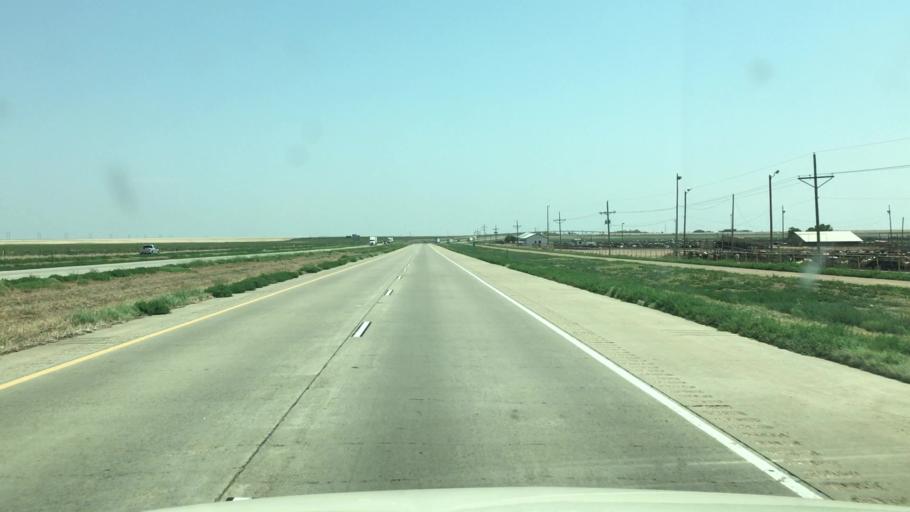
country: US
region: Texas
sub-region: Potter County
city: Bushland
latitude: 35.2088
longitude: -102.1763
